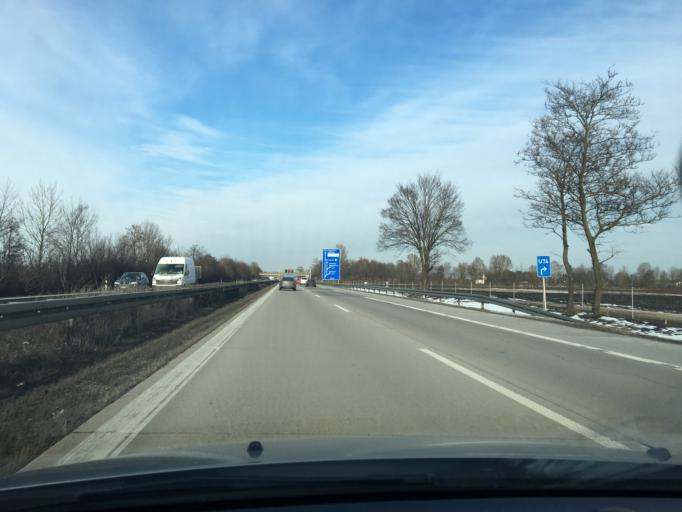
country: DE
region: Bavaria
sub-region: Upper Bavaria
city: Eching
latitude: 48.3084
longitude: 11.6045
